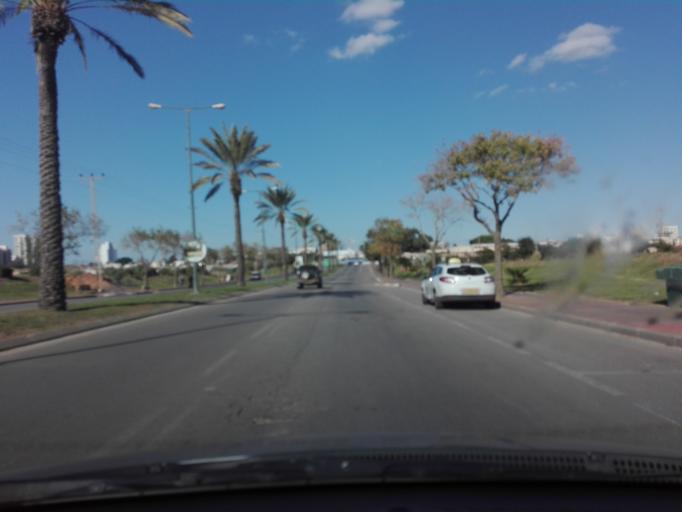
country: IL
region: Central District
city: Netanya
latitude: 32.3063
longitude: 34.8549
